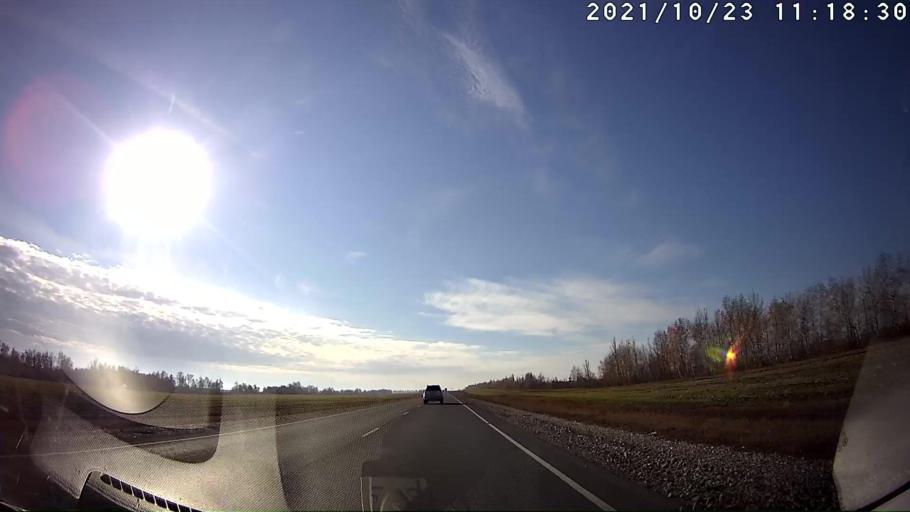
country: RU
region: Saratov
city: Kamenskiy
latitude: 50.8954
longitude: 45.5922
